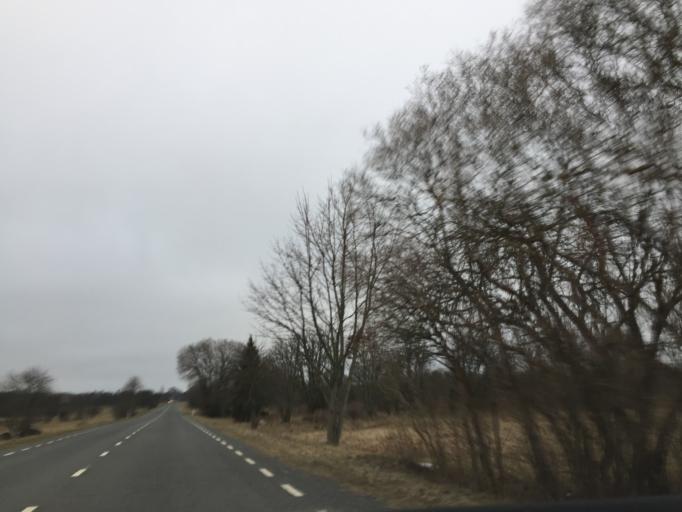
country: EE
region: Saare
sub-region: Kuressaare linn
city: Kuressaare
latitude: 58.5332
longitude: 22.3406
